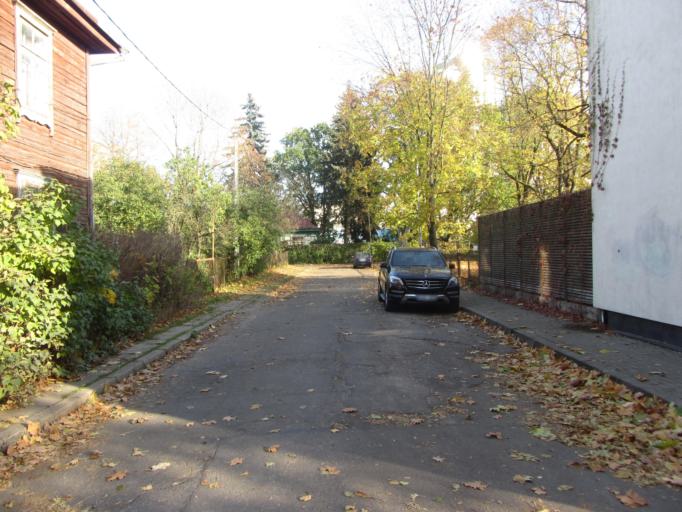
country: LT
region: Vilnius County
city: Vilkpede
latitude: 54.6800
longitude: 25.2536
